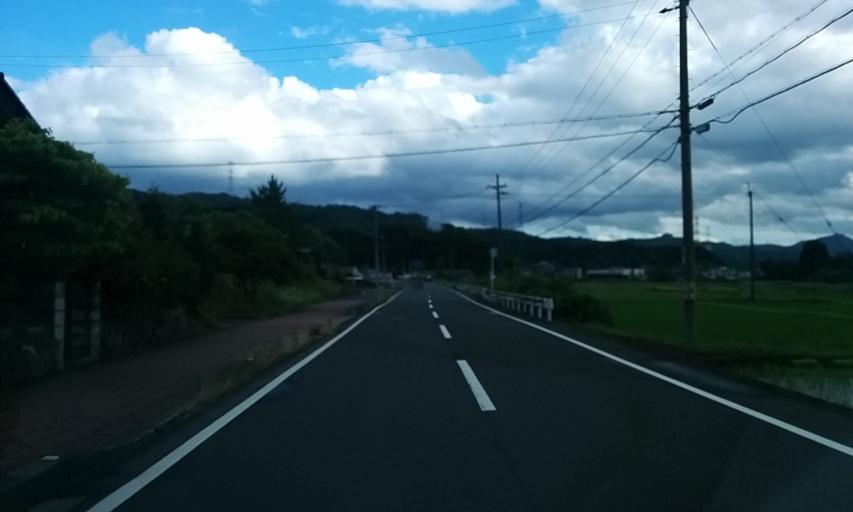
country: JP
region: Kyoto
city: Ayabe
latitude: 35.3305
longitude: 135.2928
